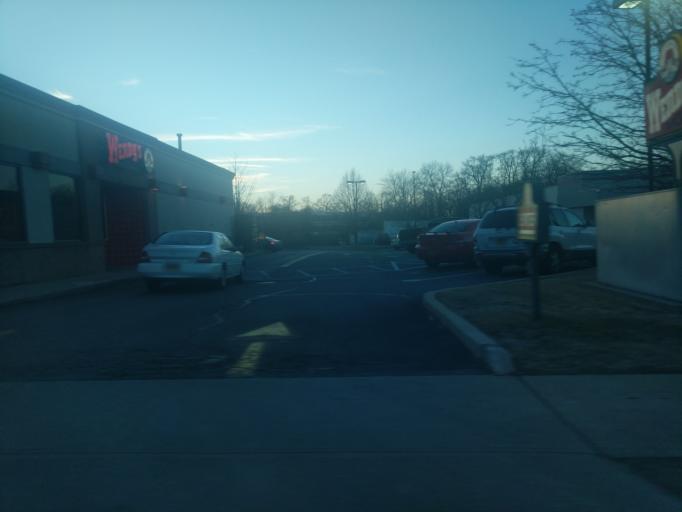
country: US
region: New York
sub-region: Nassau County
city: North Wantagh
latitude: 40.6896
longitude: -73.5089
